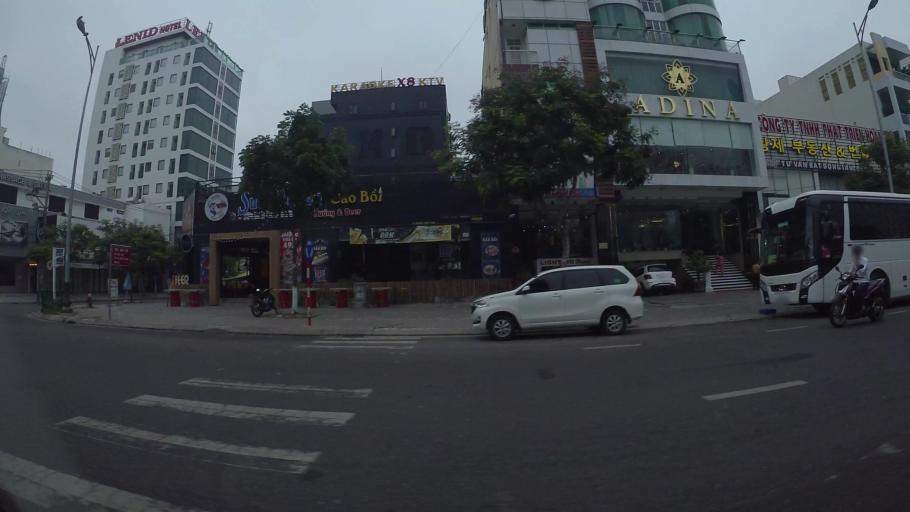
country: VN
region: Da Nang
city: Son Tra
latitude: 16.0708
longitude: 108.2365
